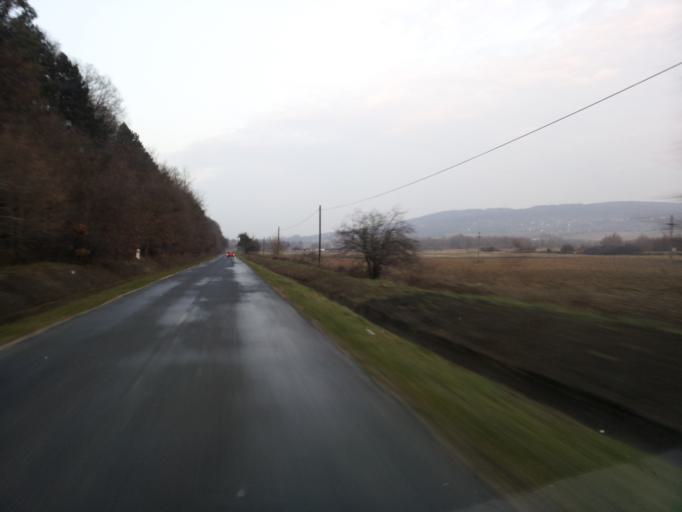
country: HU
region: Zala
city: Zalaszentgrot
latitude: 46.8836
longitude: 17.1491
